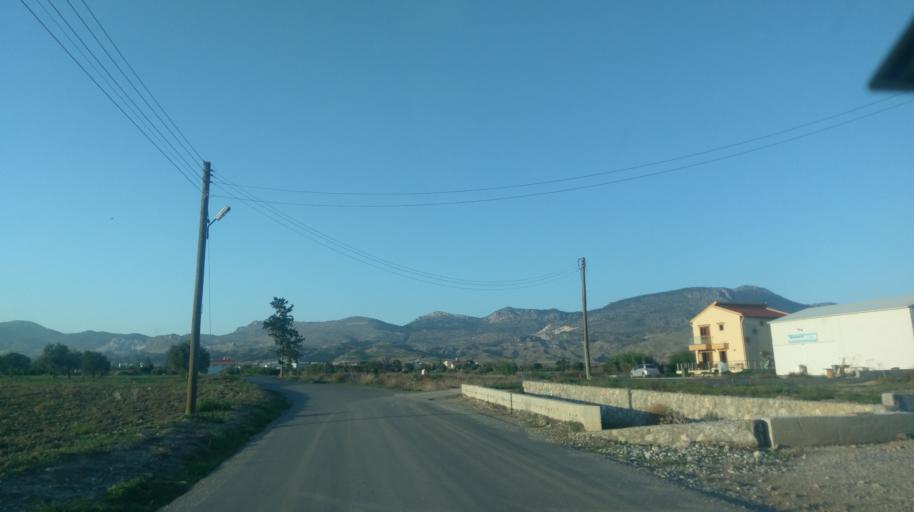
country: CY
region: Lefkosia
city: Nicosia
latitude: 35.2327
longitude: 33.5041
